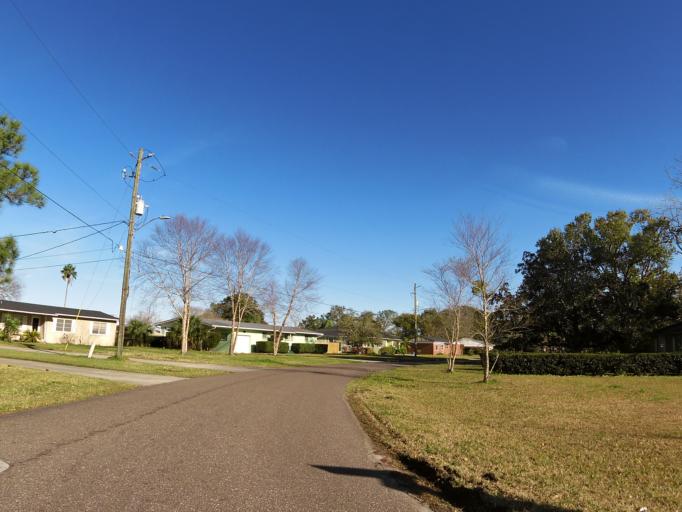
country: US
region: Florida
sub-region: Duval County
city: Jacksonville
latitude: 30.4032
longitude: -81.6730
